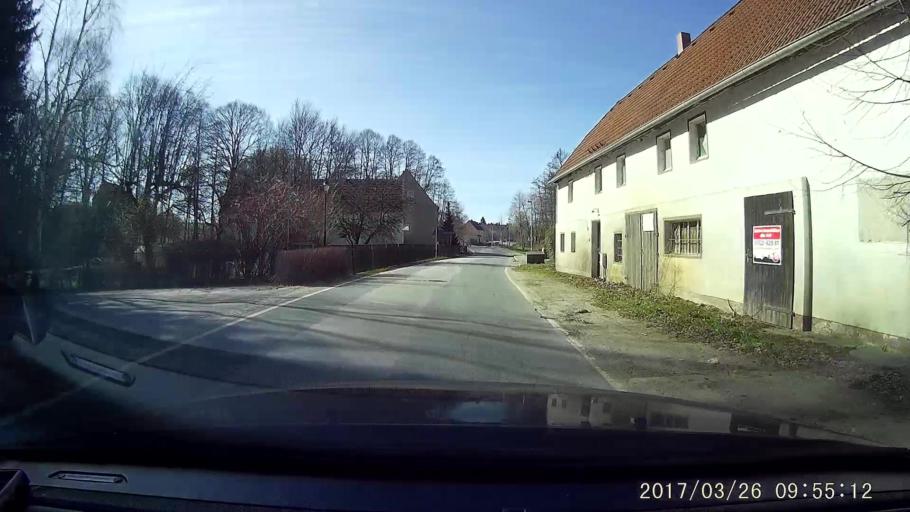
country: DE
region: Saxony
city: Sohland am Rotstein
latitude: 51.0945
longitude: 14.7421
